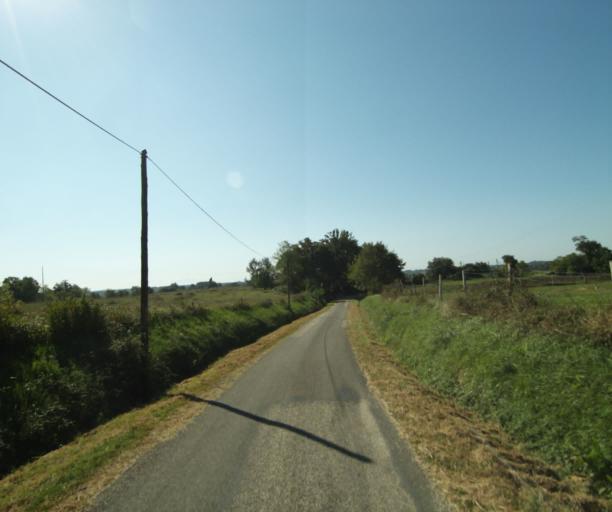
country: FR
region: Aquitaine
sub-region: Departement des Landes
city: Gabarret
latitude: 43.9491
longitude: -0.0114
